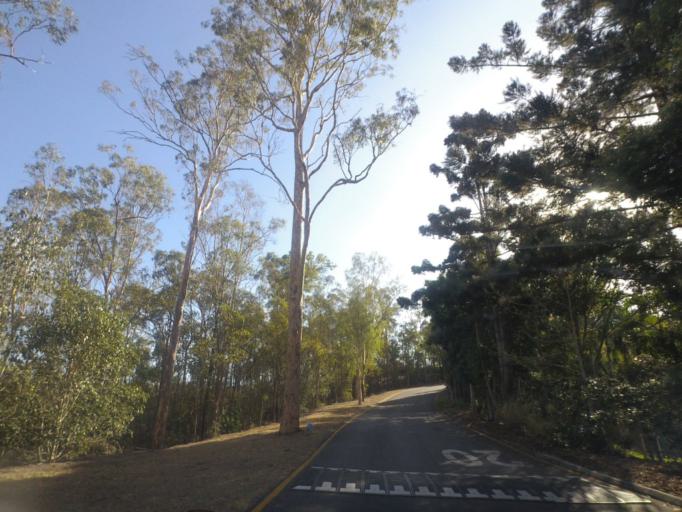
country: AU
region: Queensland
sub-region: Brisbane
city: Taringa
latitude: -27.4805
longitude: 152.9714
